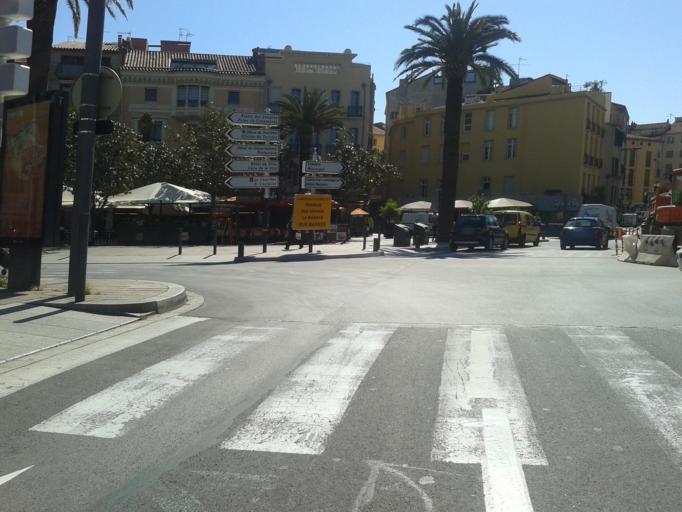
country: FR
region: Languedoc-Roussillon
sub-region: Departement des Pyrenees-Orientales
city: Perpignan
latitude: 42.6983
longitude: 2.8917
